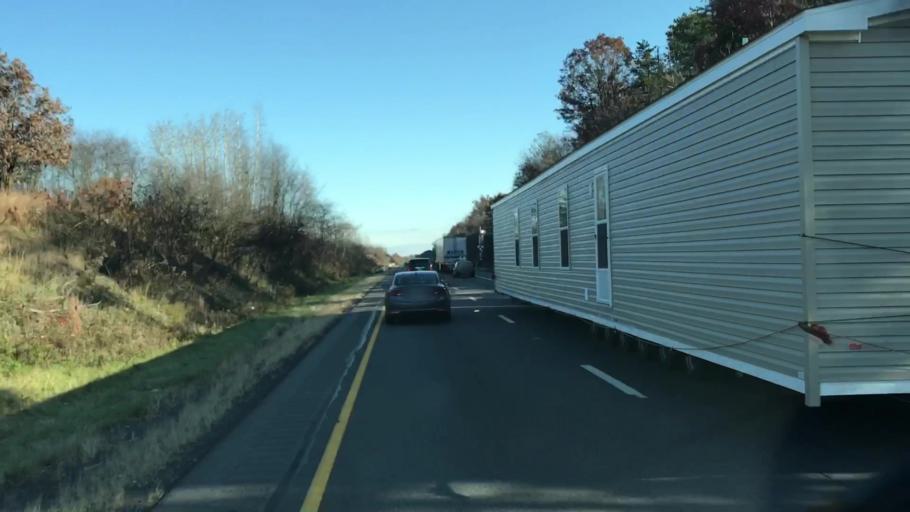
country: US
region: Pennsylvania
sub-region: Luzerne County
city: Laflin
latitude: 41.2819
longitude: -75.7902
